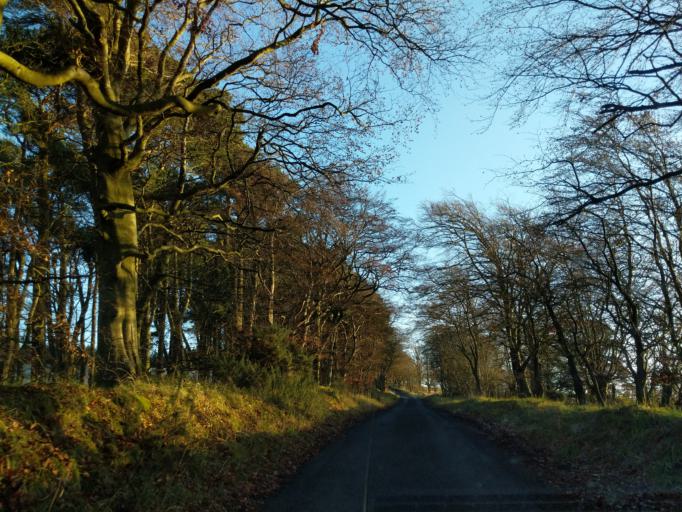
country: GB
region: Scotland
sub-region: Edinburgh
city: Balerno
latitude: 55.8609
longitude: -3.3673
